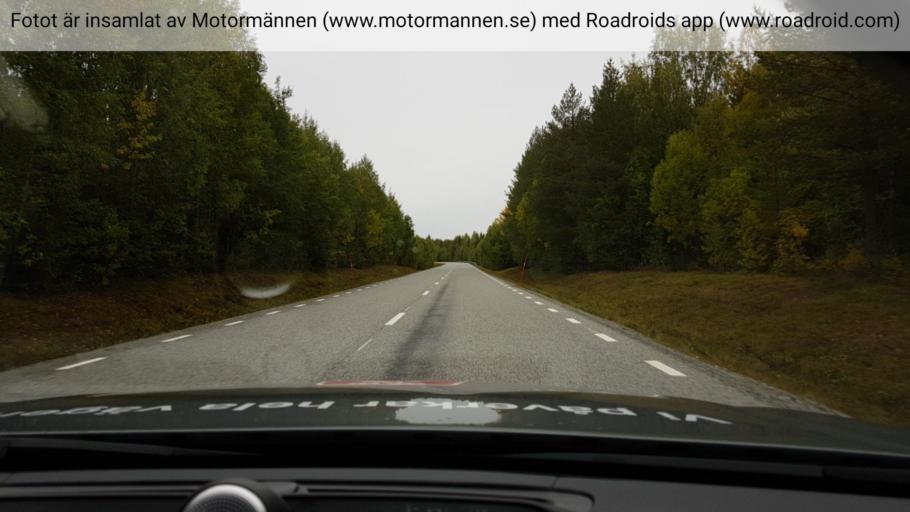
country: SE
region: Jaemtland
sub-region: Stroemsunds Kommun
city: Stroemsund
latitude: 64.1892
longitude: 15.6391
